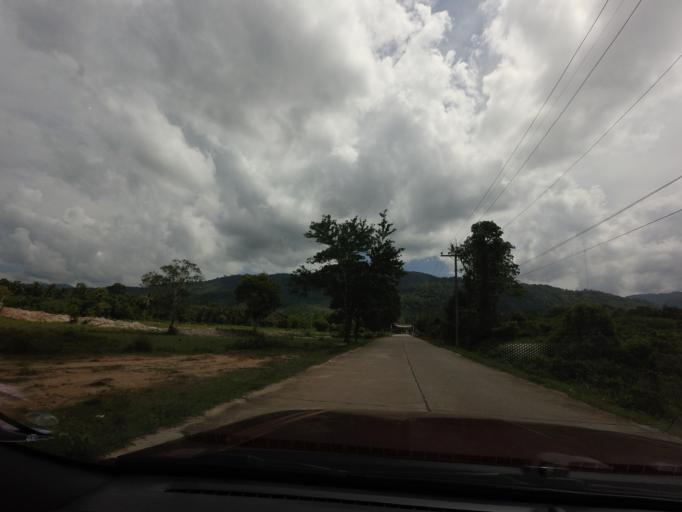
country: TH
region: Narathiwat
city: Bacho
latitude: 6.4856
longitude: 101.6599
